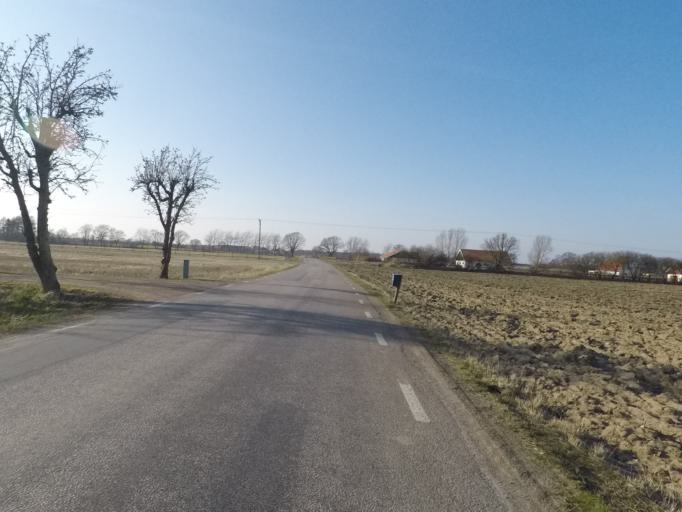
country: SE
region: Skane
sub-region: Hoganas Kommun
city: Hoganas
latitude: 56.2321
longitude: 12.6639
